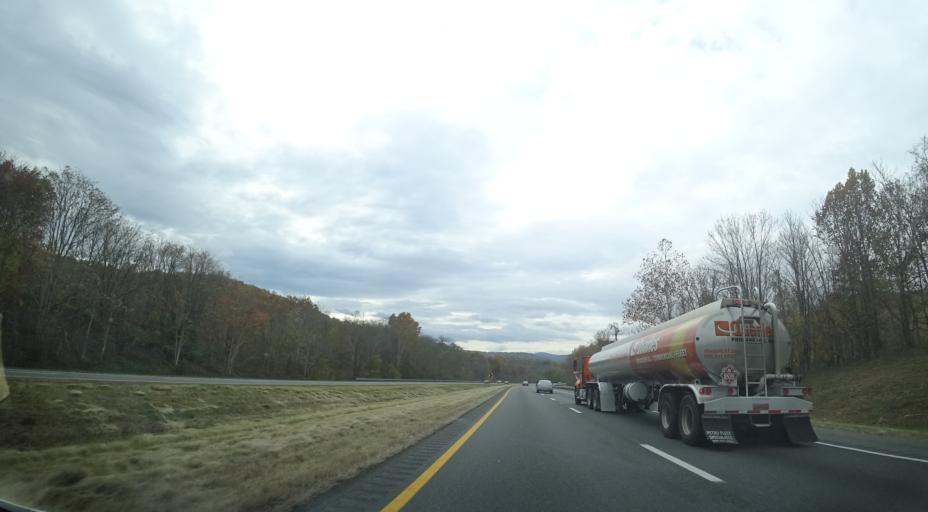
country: US
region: Virginia
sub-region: Fauquier County
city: Marshall
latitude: 38.9086
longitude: -77.9641
